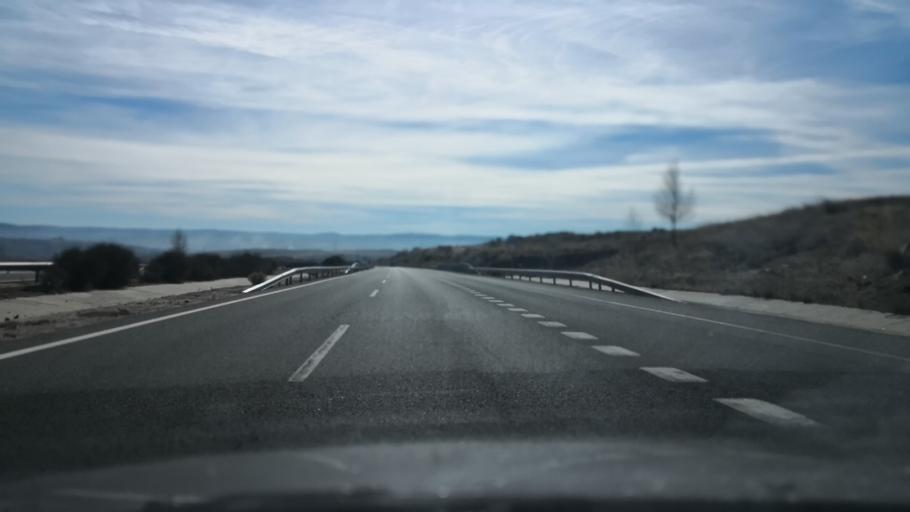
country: ES
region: Castille and Leon
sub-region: Provincia de Avila
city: Martiherrero
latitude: 40.6944
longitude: -4.7397
